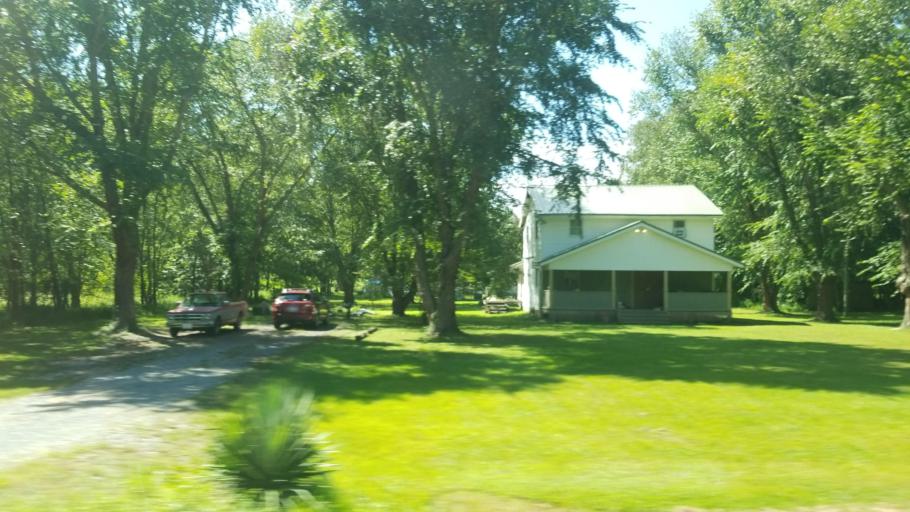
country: US
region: Illinois
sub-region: Williamson County
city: Johnston City
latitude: 37.7903
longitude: -88.9235
